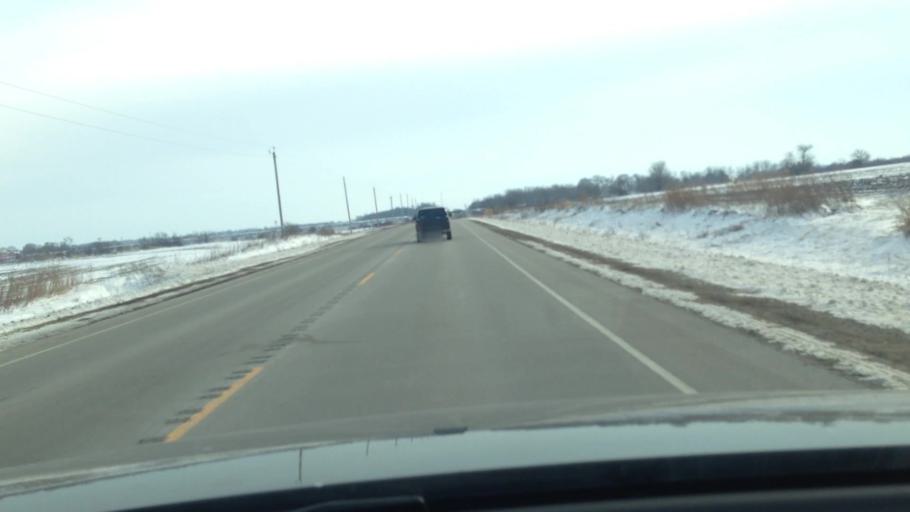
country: US
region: Illinois
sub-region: McHenry County
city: Hebron
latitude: 42.5051
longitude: -88.4425
